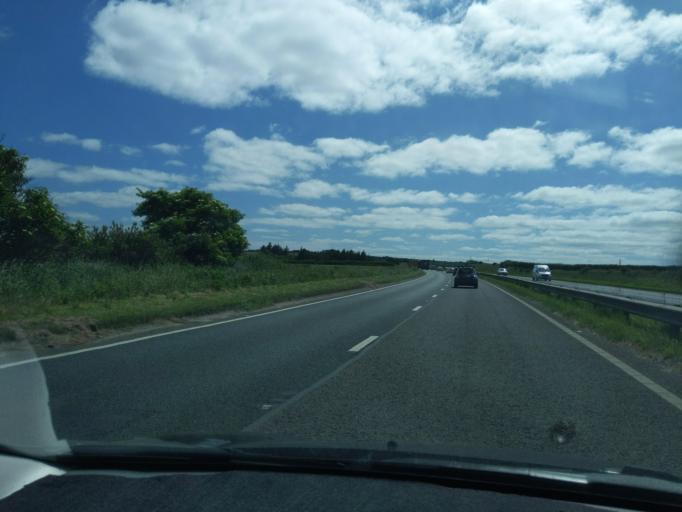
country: GB
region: England
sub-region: Cornwall
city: Probus
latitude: 50.3595
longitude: -4.9884
